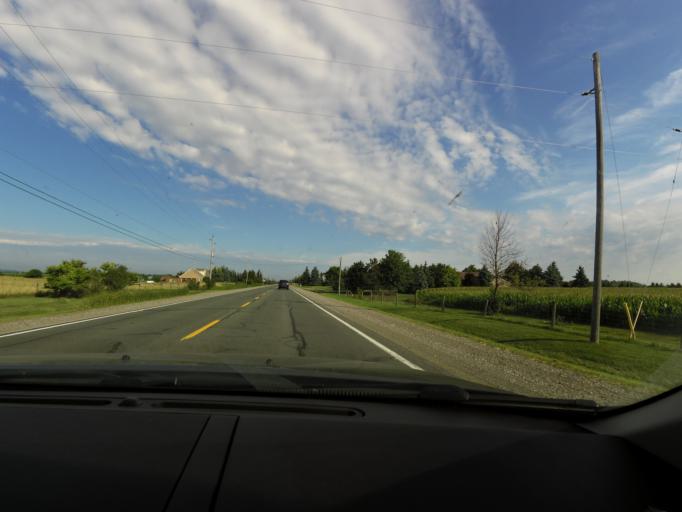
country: CA
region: Ontario
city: Brampton
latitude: 43.7849
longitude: -79.8229
